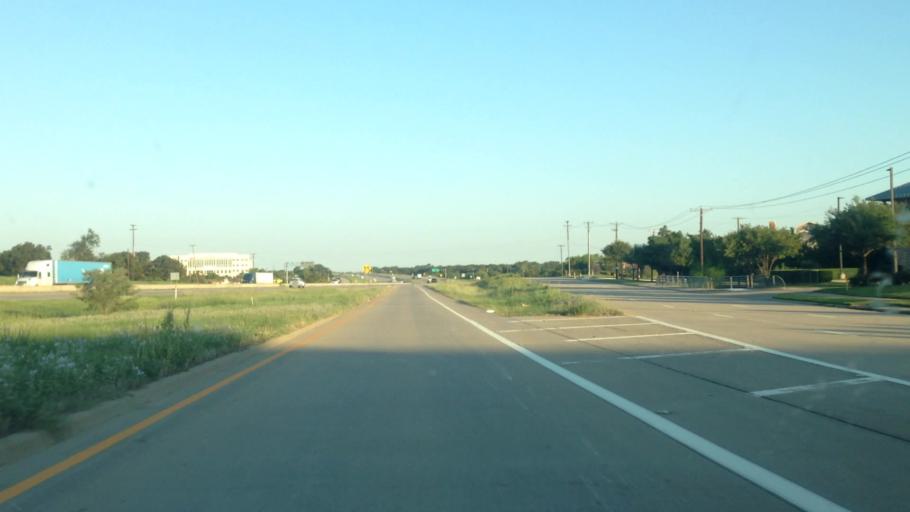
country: US
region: Texas
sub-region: Tarrant County
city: Southlake
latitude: 32.9545
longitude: -97.1371
